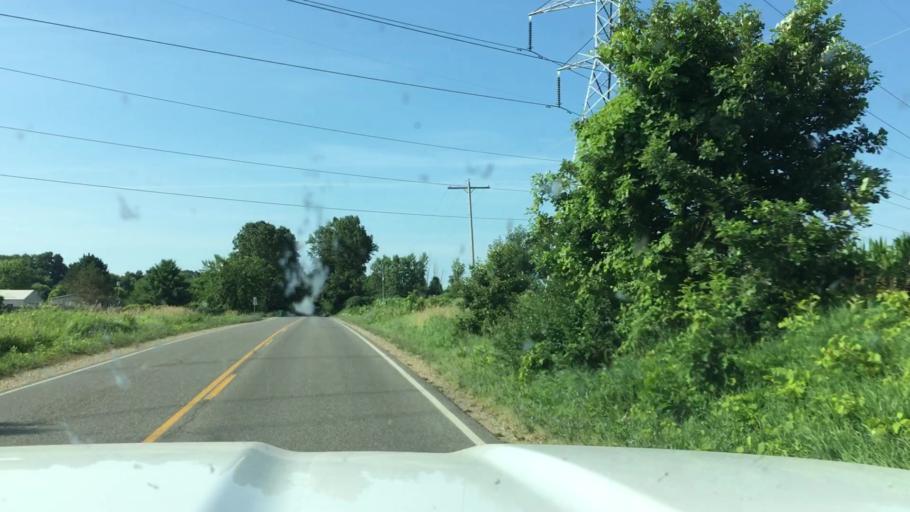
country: US
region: Michigan
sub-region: Barry County
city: Stony Point
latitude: 42.4395
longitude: -85.4545
